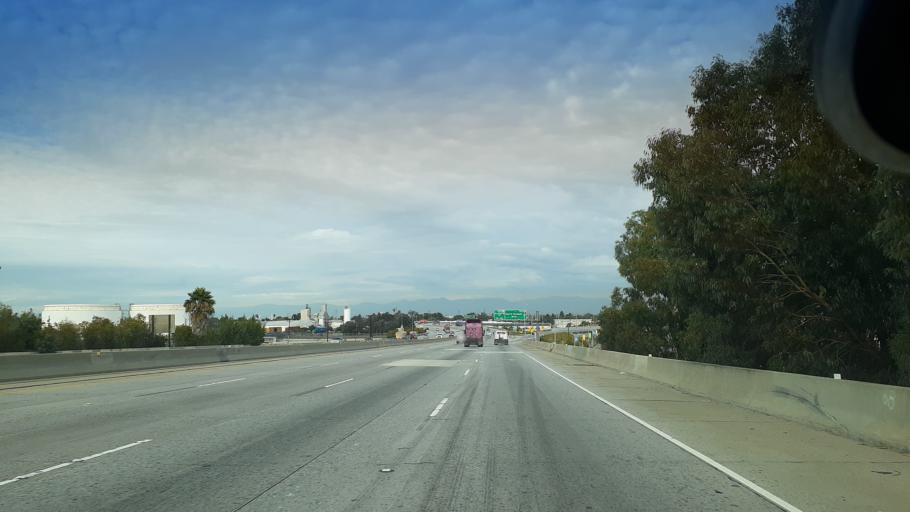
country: US
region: California
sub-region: Los Angeles County
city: San Pedro
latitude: 33.7681
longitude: -118.2805
